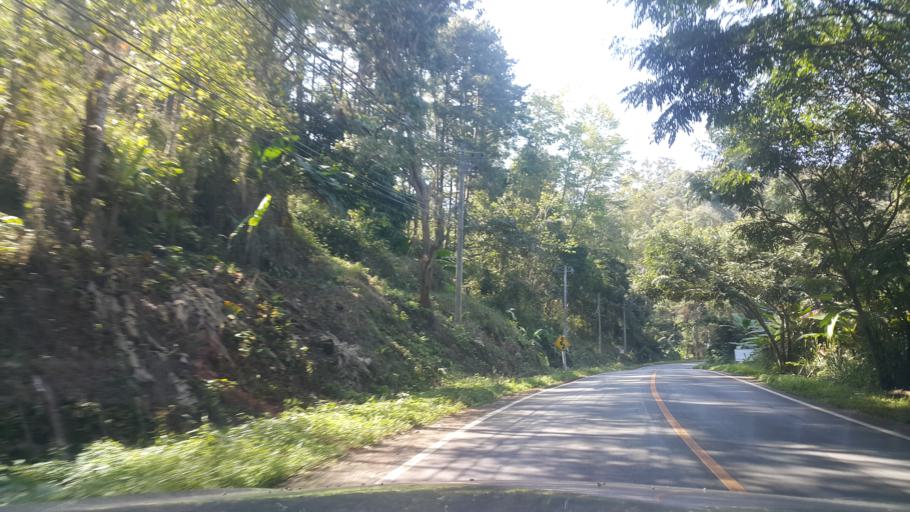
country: TH
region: Chiang Mai
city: Samoeng
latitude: 18.8766
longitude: 98.7909
